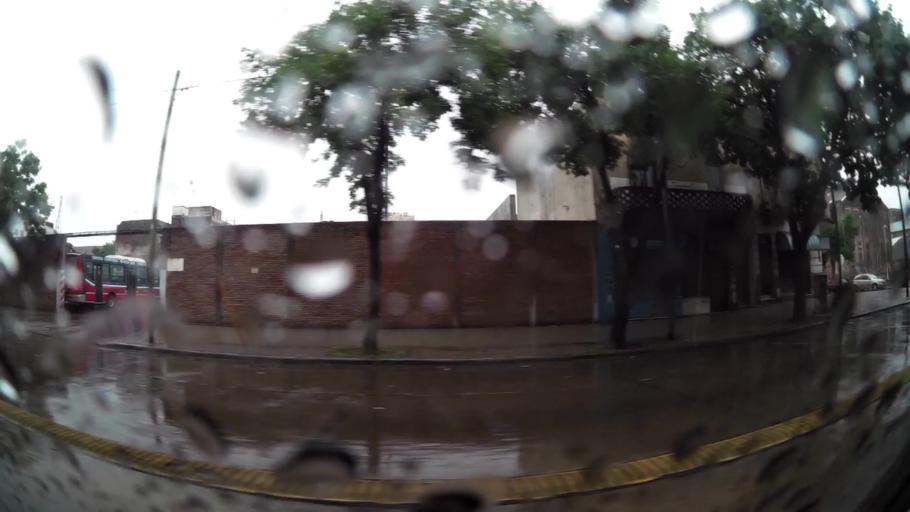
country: AR
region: Buenos Aires
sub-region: Partido de Avellaneda
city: Avellaneda
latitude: -34.6415
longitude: -58.3691
